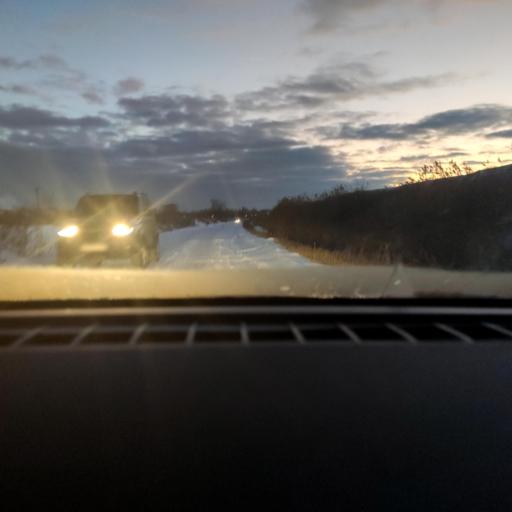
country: RU
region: Voronezj
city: Voronezh
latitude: 51.6194
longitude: 39.2213
